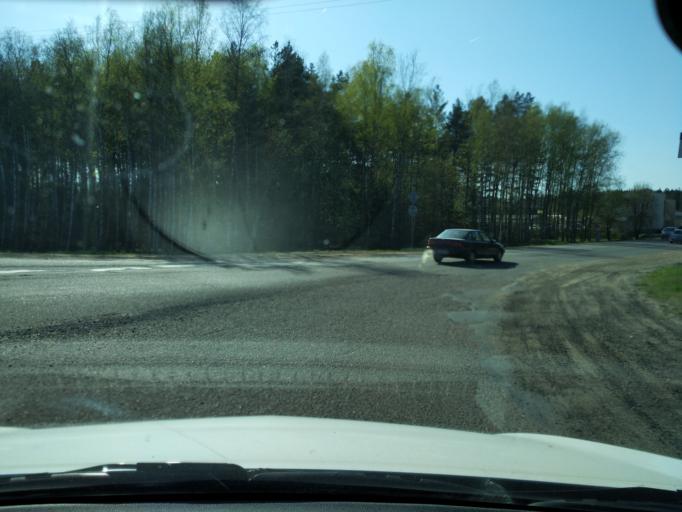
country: BY
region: Minsk
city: Lyeskawka
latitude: 53.9582
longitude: 27.7244
